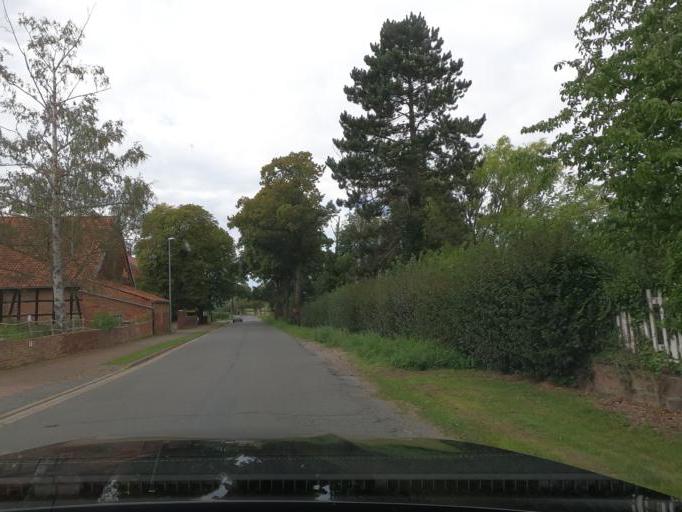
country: DE
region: Lower Saxony
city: Ilsede
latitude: 52.2175
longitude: 10.1614
